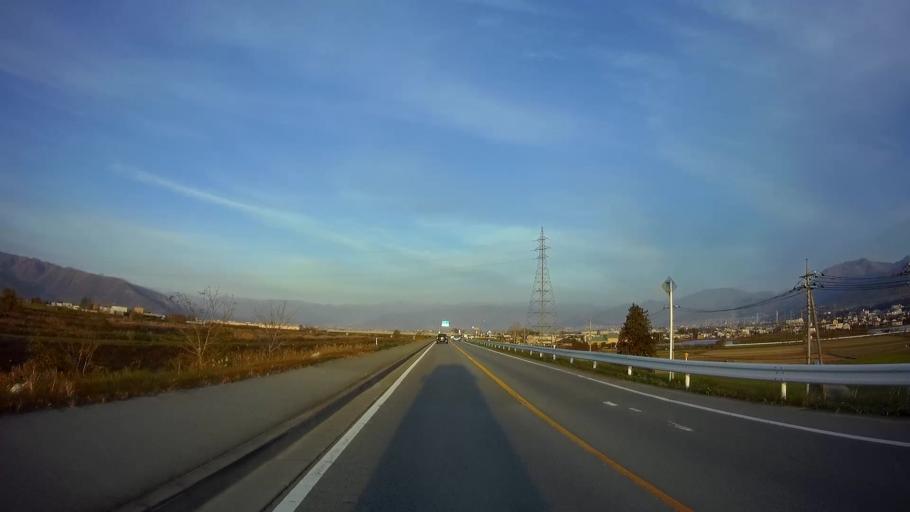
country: JP
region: Yamanashi
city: Isawa
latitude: 35.6091
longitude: 138.5933
